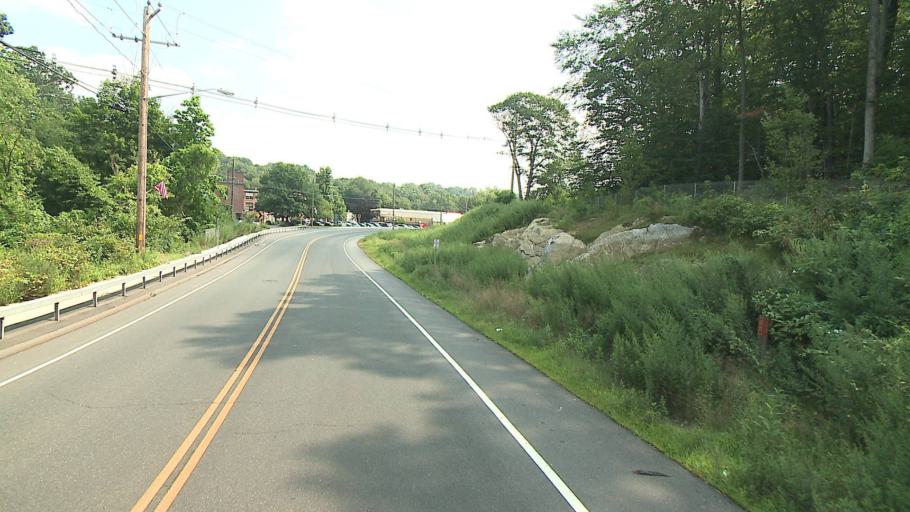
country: US
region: Connecticut
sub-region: Litchfield County
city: Oakville
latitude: 41.5898
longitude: -73.0980
